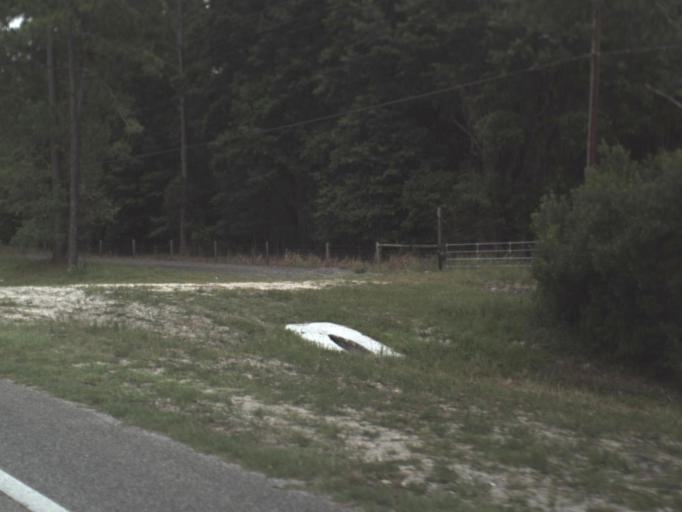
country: US
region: Florida
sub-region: Alachua County
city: Waldo
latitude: 29.7415
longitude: -82.2336
